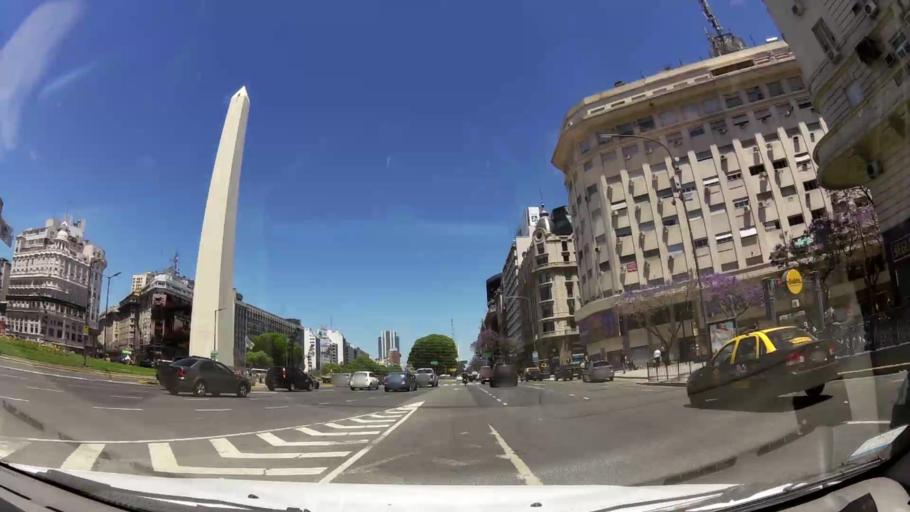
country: AR
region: Buenos Aires F.D.
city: Buenos Aires
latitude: -34.6031
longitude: -58.3822
